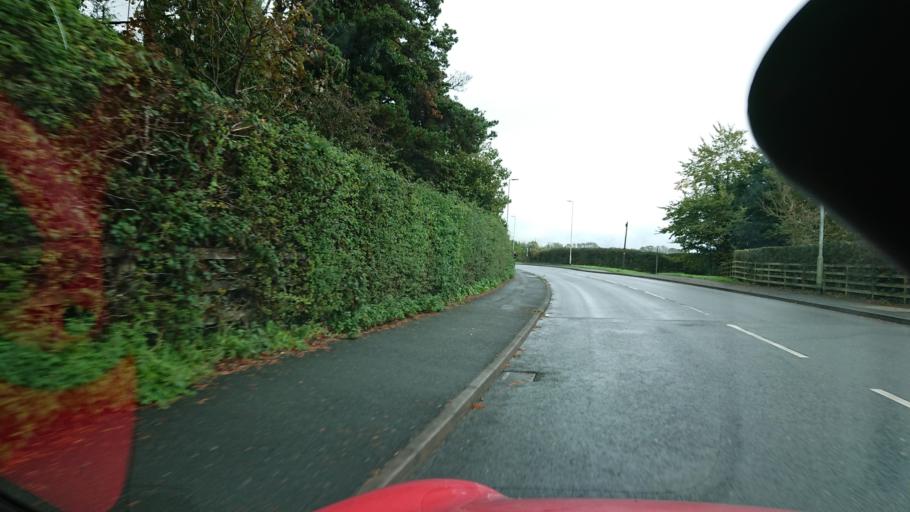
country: GB
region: England
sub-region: Devon
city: Plympton
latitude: 50.4182
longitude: -4.1090
